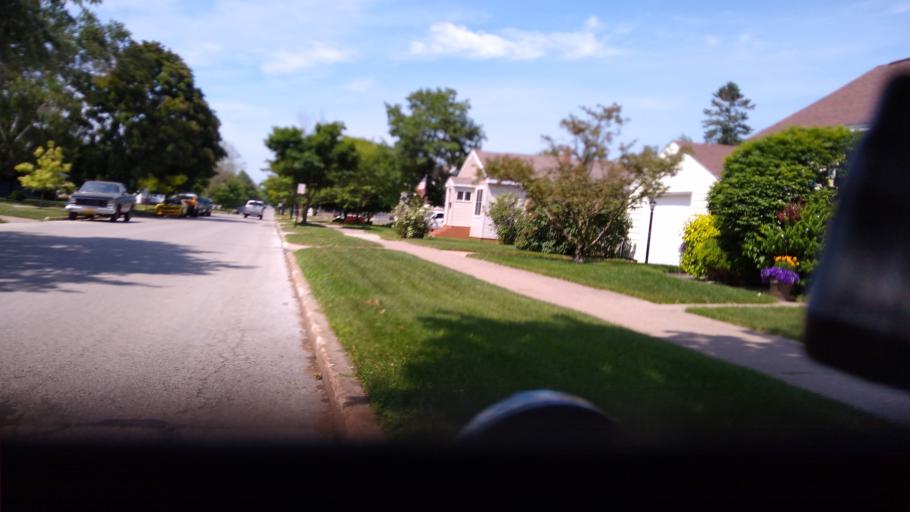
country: US
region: Michigan
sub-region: Delta County
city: Escanaba
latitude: 45.7363
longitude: -87.0739
